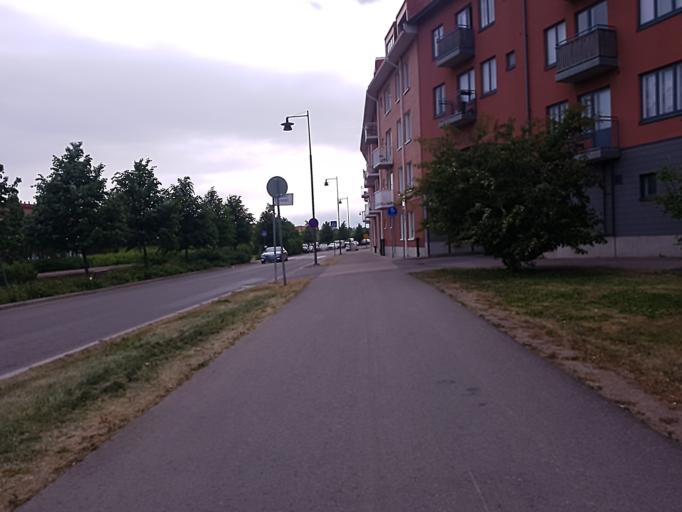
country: FI
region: Uusimaa
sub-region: Helsinki
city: Vantaa
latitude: 60.2814
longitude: 24.9639
